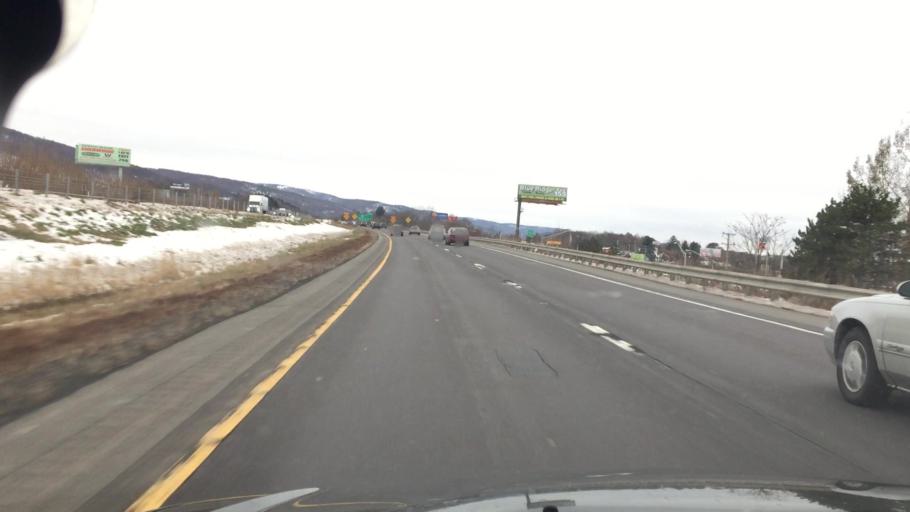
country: US
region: Pennsylvania
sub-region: Luzerne County
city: Georgetown
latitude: 41.2254
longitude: -75.8761
